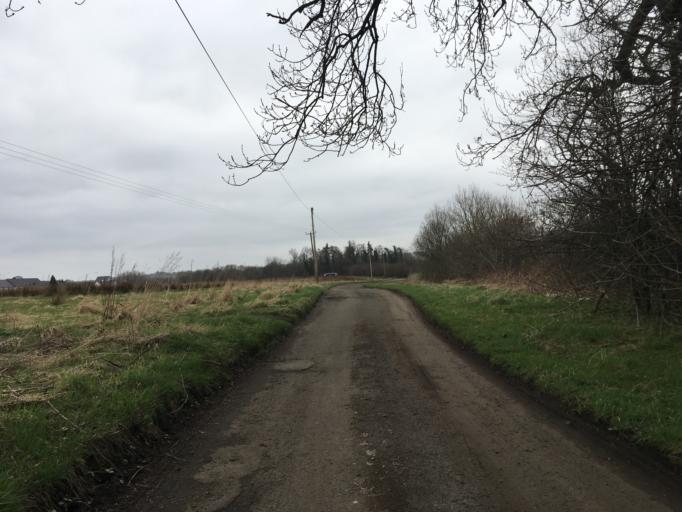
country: GB
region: Scotland
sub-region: Stirling
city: Bridge of Allan
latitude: 56.1377
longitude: -3.9668
